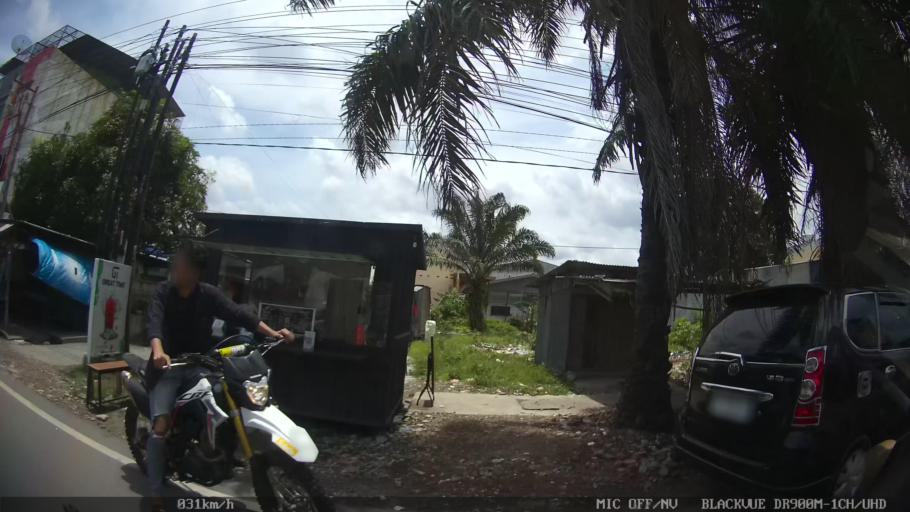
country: ID
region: North Sumatra
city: Medan
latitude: 3.6159
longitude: 98.6979
